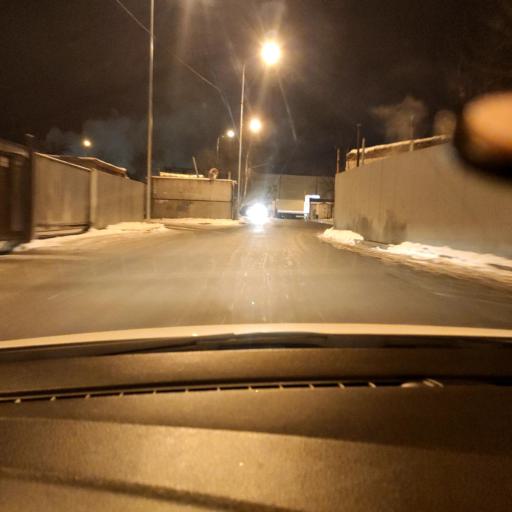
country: RU
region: Tatarstan
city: Staroye Arakchino
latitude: 55.8287
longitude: 49.0428
